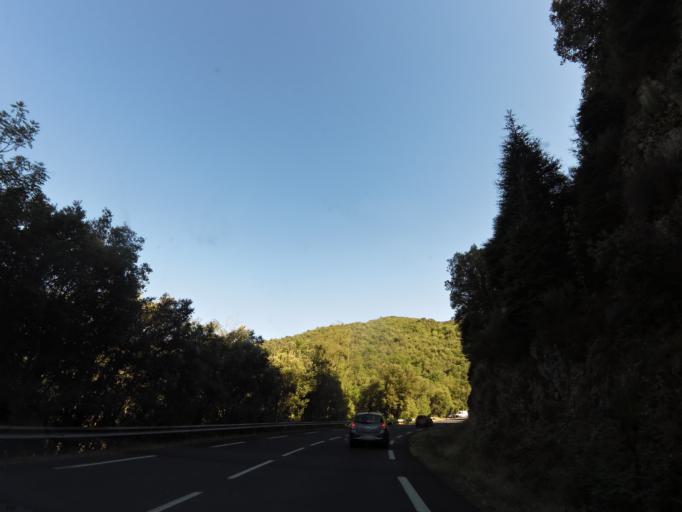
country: FR
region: Languedoc-Roussillon
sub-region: Departement du Gard
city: Valleraugue
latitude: 44.0467
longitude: 3.6860
